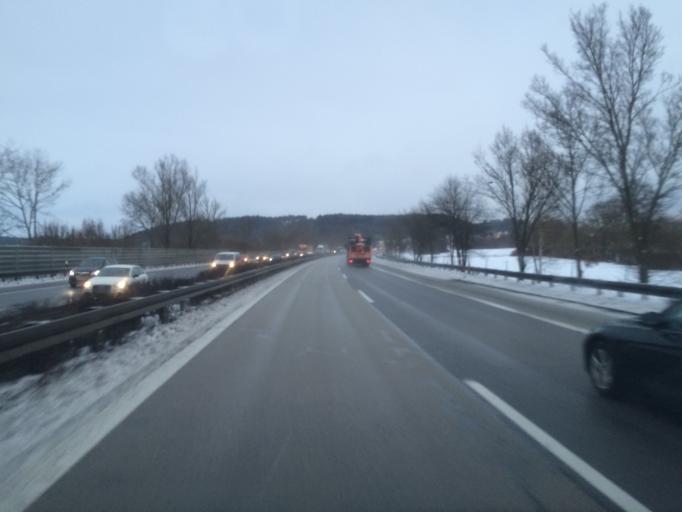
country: DE
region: Bavaria
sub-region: Upper Palatinate
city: Lappersdorf
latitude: 49.0655
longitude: 12.0921
